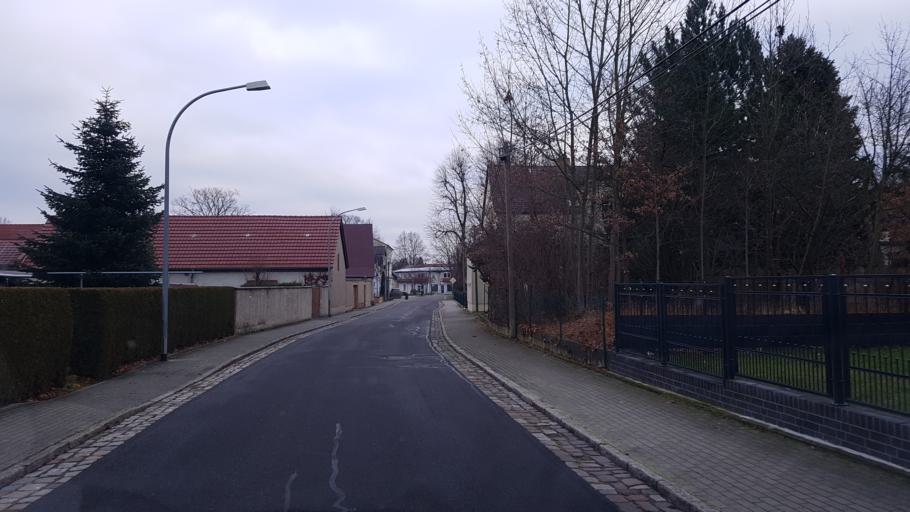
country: DE
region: Brandenburg
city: Schipkau
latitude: 51.5436
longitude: 13.8931
